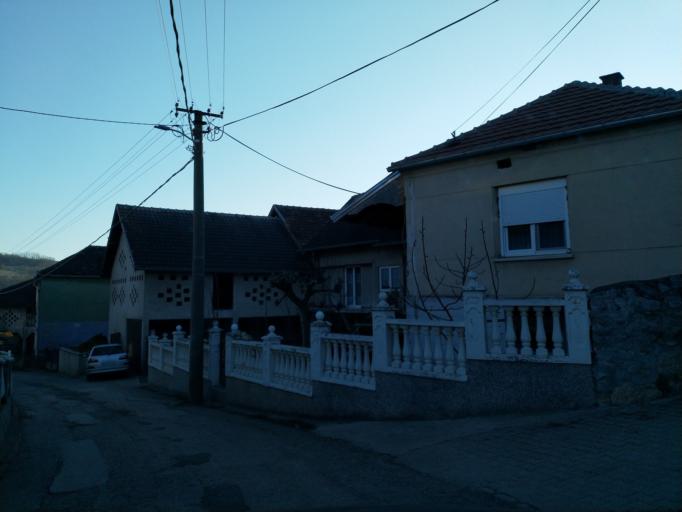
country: RS
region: Central Serbia
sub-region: Pomoravski Okrug
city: Paracin
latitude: 43.9354
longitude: 21.5206
